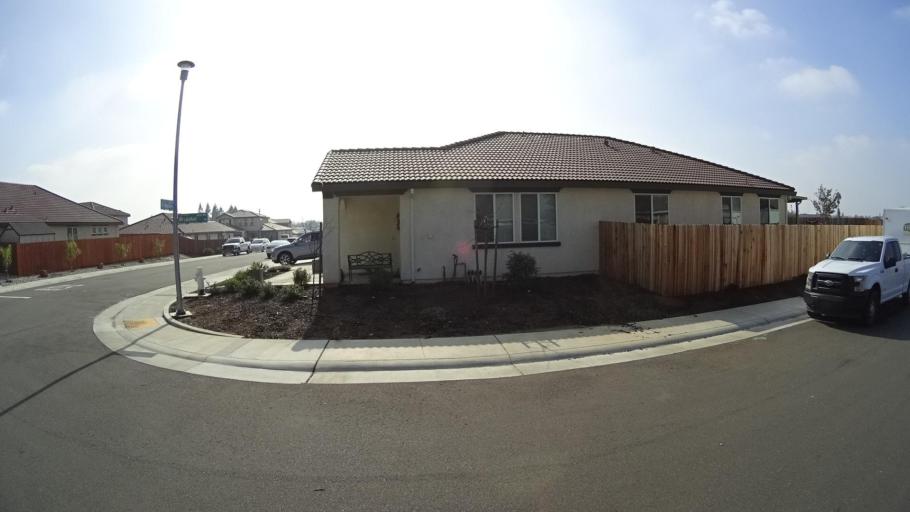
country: US
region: California
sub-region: Sacramento County
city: Vineyard
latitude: 38.4508
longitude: -121.3661
